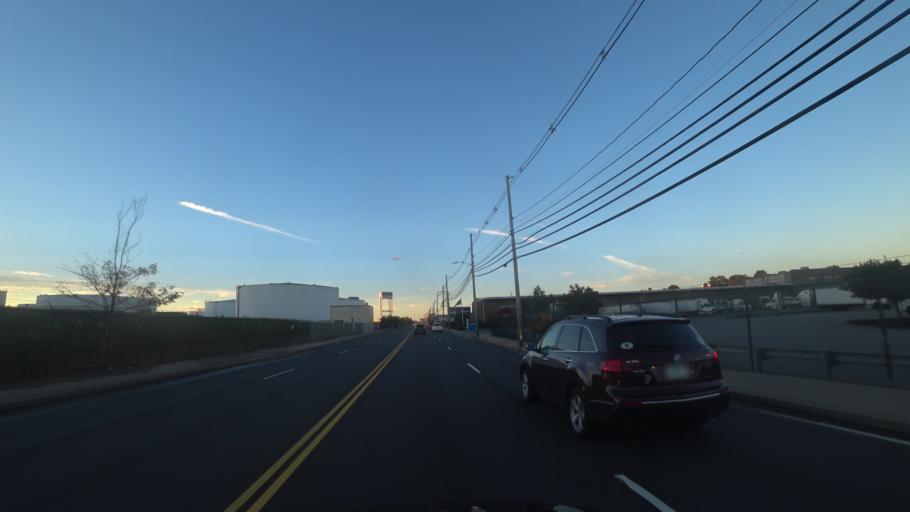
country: US
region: Massachusetts
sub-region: Suffolk County
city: Chelsea
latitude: 42.3946
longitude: -71.0216
